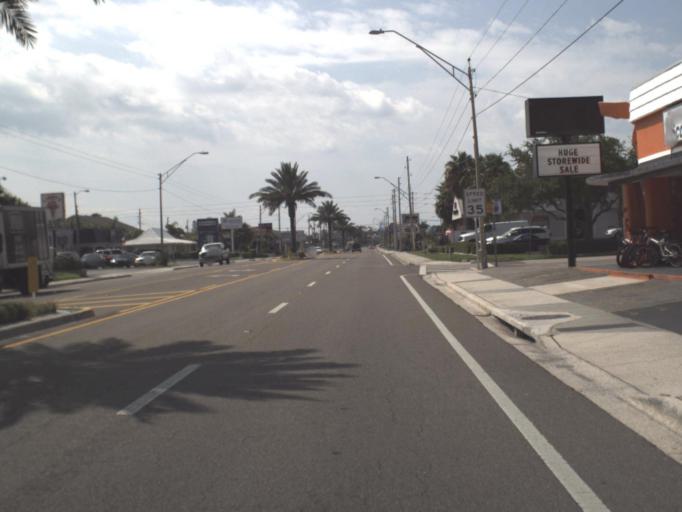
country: US
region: Florida
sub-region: Pinellas County
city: Saint Pete Beach
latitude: 27.7369
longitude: -82.7481
